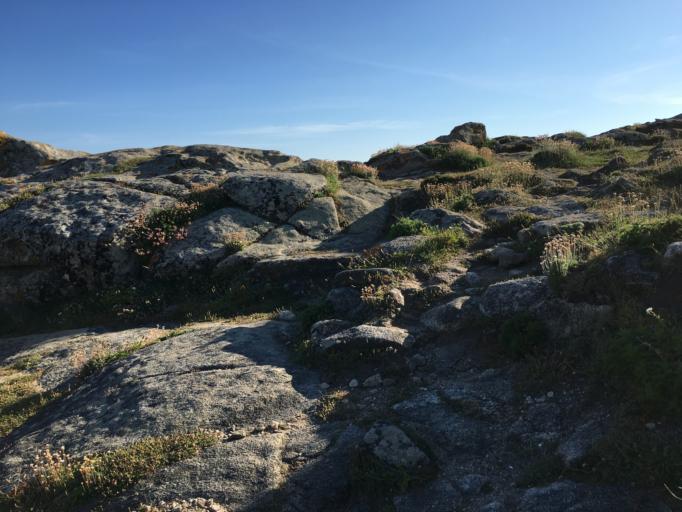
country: ES
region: Galicia
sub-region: Provincia da Coruna
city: Porto do Son
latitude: 42.6942
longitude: -9.0317
